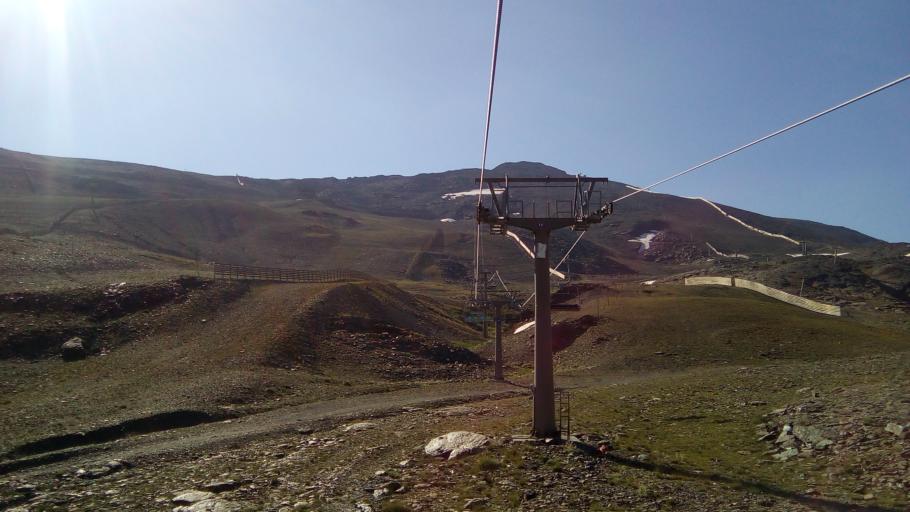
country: ES
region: Andalusia
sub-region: Provincia de Granada
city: Capileira
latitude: 37.0673
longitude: -3.3814
